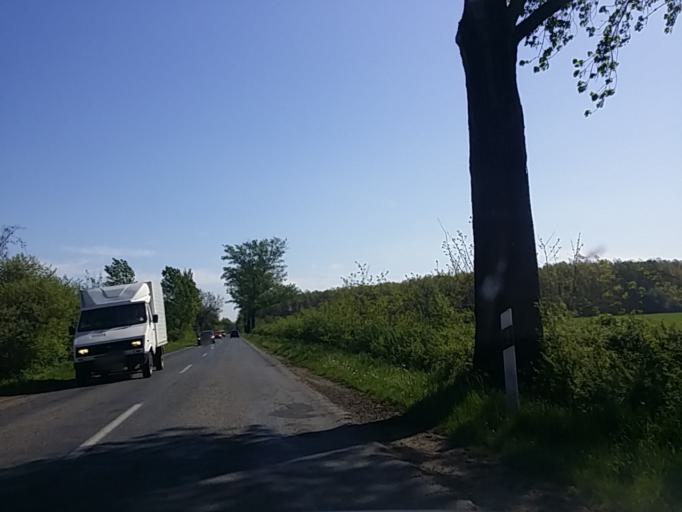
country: HU
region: Bekes
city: Doboz
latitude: 46.7157
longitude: 21.1912
